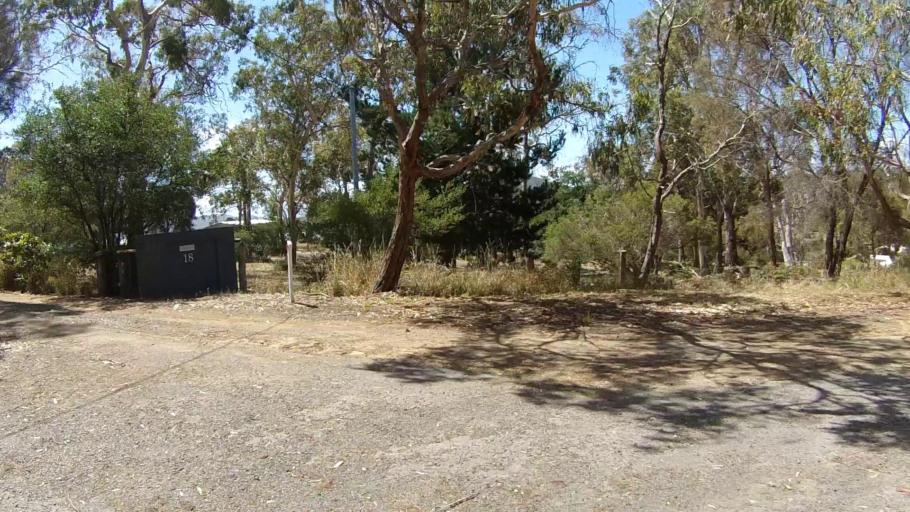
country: AU
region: Tasmania
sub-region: Clarence
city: Sandford
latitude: -42.9912
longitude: 147.4763
